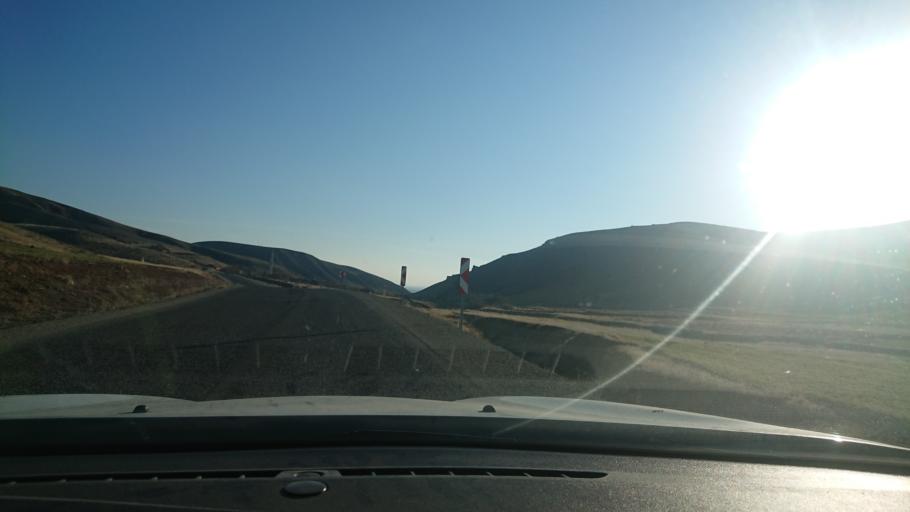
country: TR
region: Aksaray
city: Acipinar
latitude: 38.6966
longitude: 33.7494
